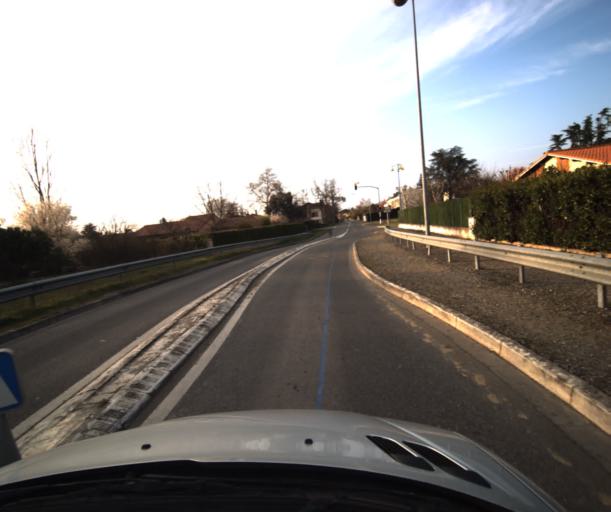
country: FR
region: Midi-Pyrenees
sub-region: Departement de la Haute-Garonne
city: Fonbeauzard
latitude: 43.6851
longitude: 1.4396
